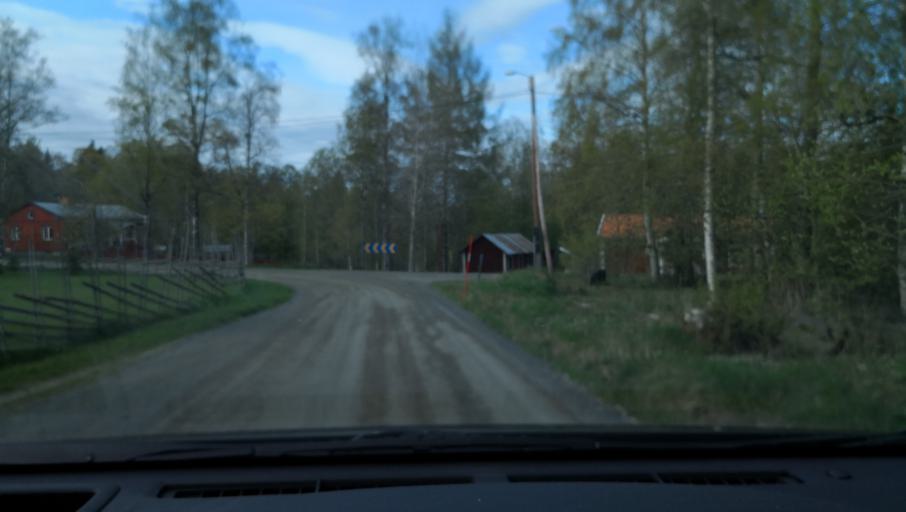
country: SE
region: Dalarna
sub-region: Saters Kommun
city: Saeter
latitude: 60.2645
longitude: 15.8296
